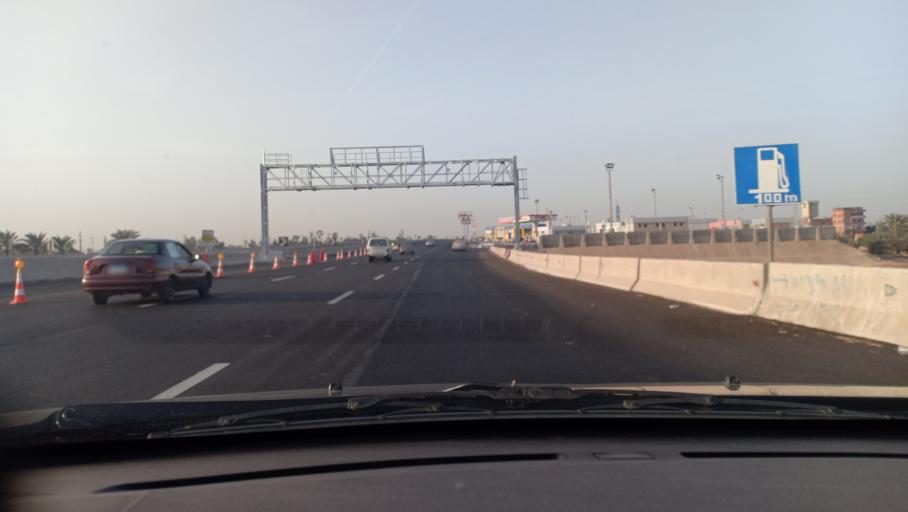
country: EG
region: Muhafazat al Qalyubiyah
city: Toukh
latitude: 30.3030
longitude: 31.2198
